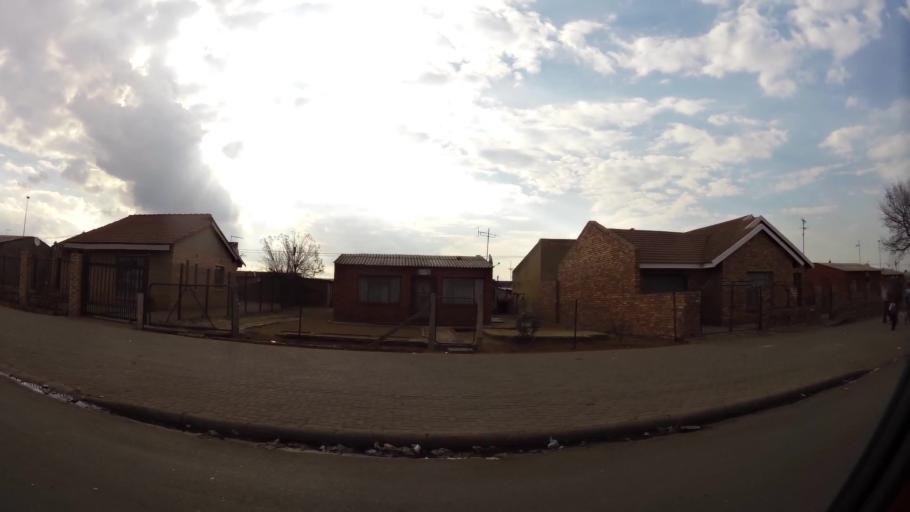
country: ZA
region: Gauteng
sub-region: Sedibeng District Municipality
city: Vanderbijlpark
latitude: -26.6860
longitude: 27.8718
